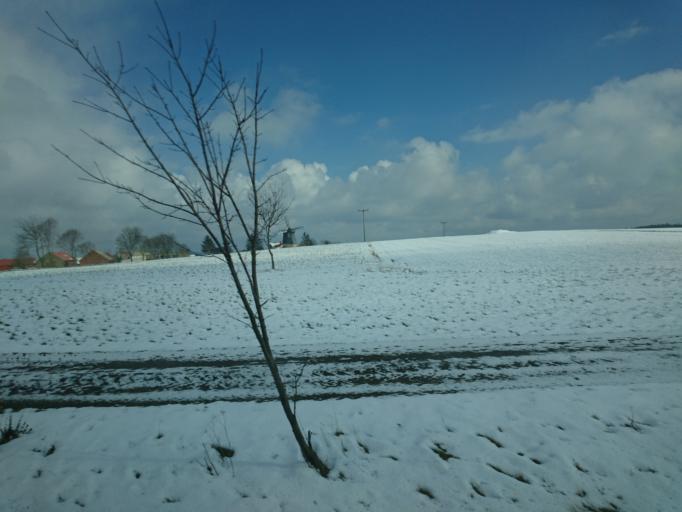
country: DE
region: Thuringia
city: Dreba
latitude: 50.6836
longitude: 11.7796
